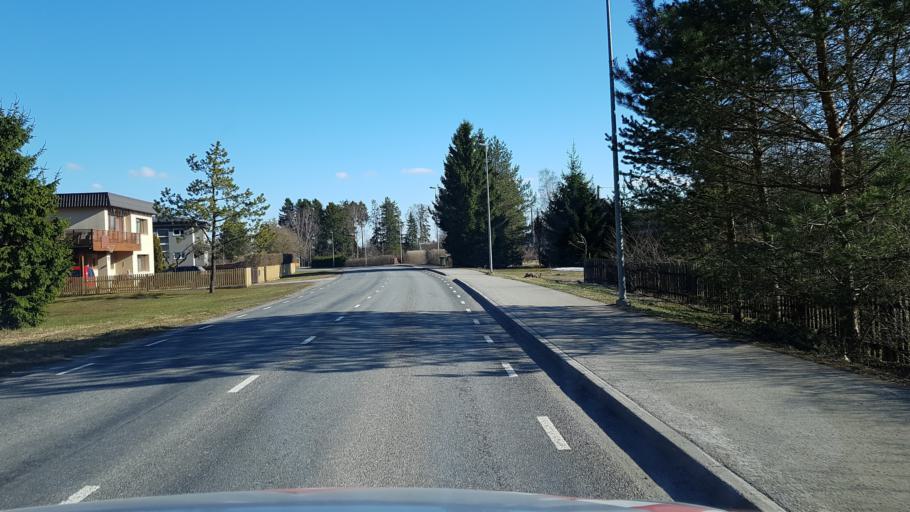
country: EE
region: Laeaene-Virumaa
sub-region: Haljala vald
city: Haljala
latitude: 59.4428
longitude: 26.2552
